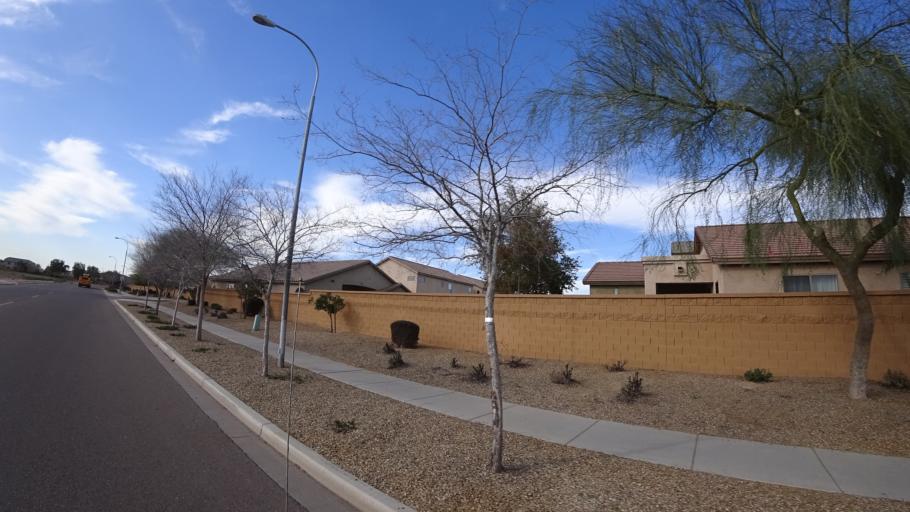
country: US
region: Arizona
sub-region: Maricopa County
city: Tolleson
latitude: 33.4101
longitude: -112.2764
